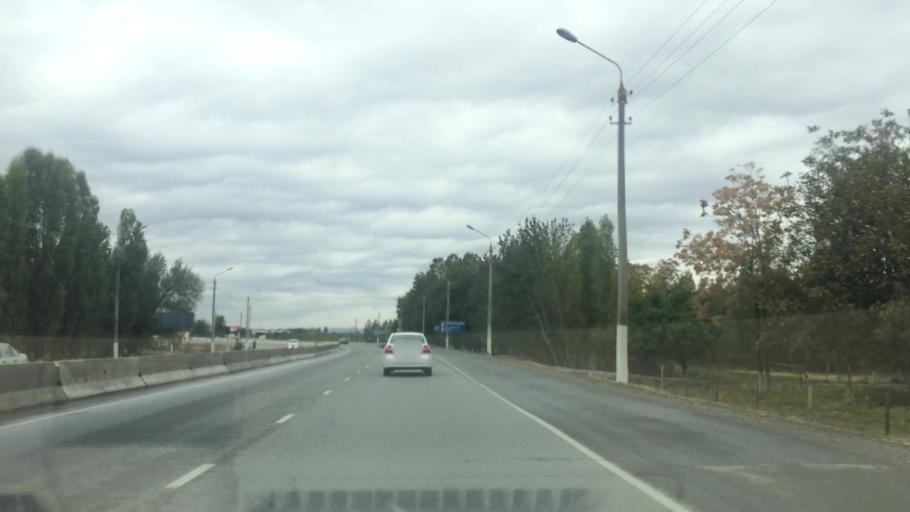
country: UZ
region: Jizzax
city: Jizzax
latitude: 39.9784
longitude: 67.5650
